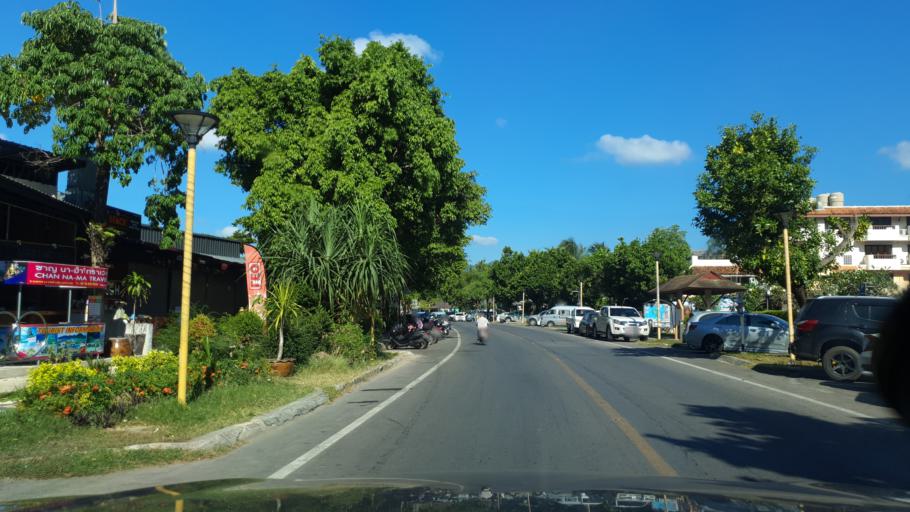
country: TH
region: Phangnga
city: Ban Ao Nang
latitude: 8.0388
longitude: 98.8160
